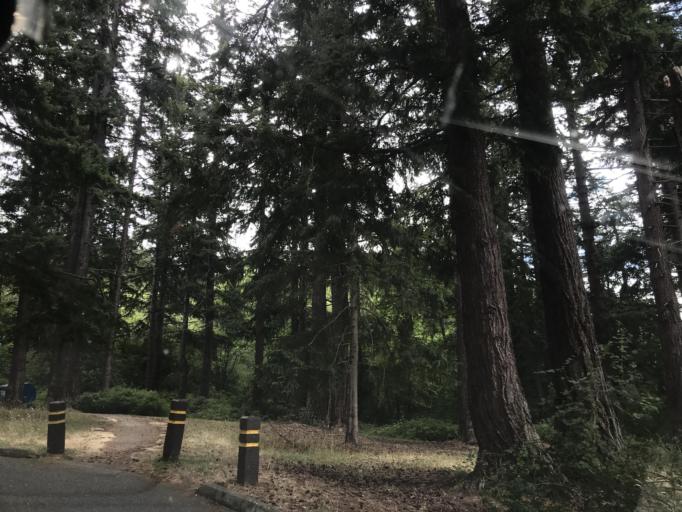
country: US
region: Washington
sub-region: Whatcom County
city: Bellingham
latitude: 48.7136
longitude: -122.4971
